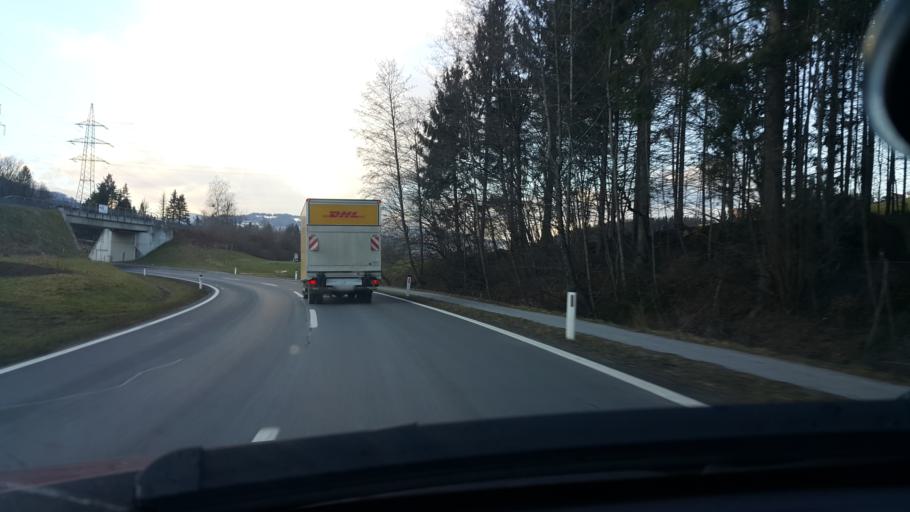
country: AT
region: Styria
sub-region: Politischer Bezirk Deutschlandsberg
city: Hollenegg
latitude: 46.7924
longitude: 15.2363
